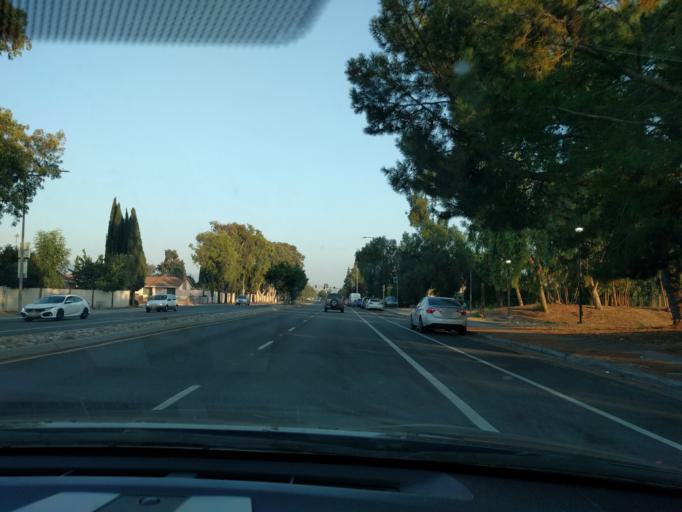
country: US
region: California
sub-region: Santa Clara County
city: Alum Rock
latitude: 37.3685
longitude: -121.8535
